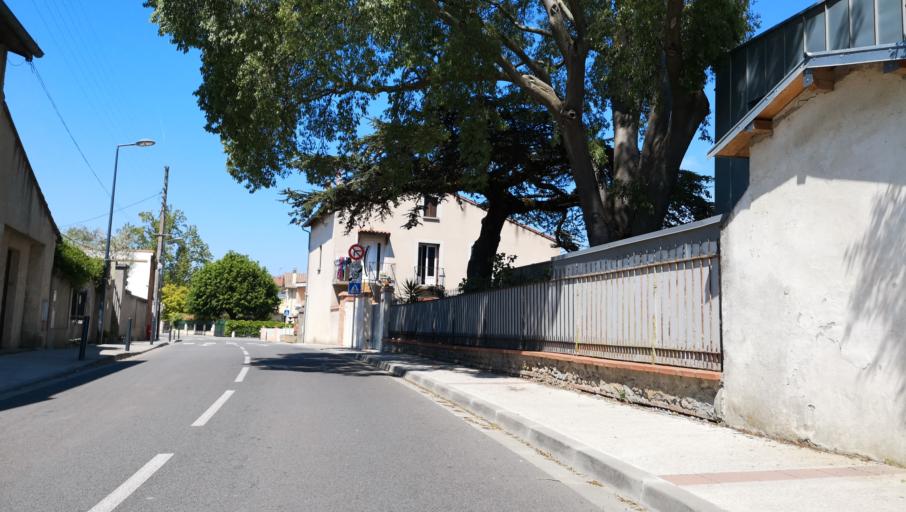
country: FR
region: Midi-Pyrenees
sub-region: Departement de la Haute-Garonne
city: Blagnac
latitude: 43.6406
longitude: 1.3913
